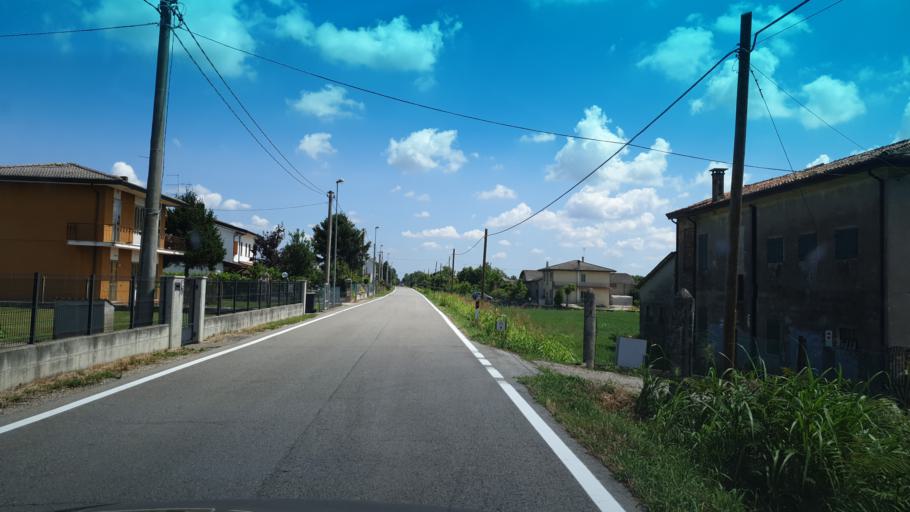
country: IT
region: Veneto
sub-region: Provincia di Padova
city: Stanghella
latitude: 45.1432
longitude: 11.7857
